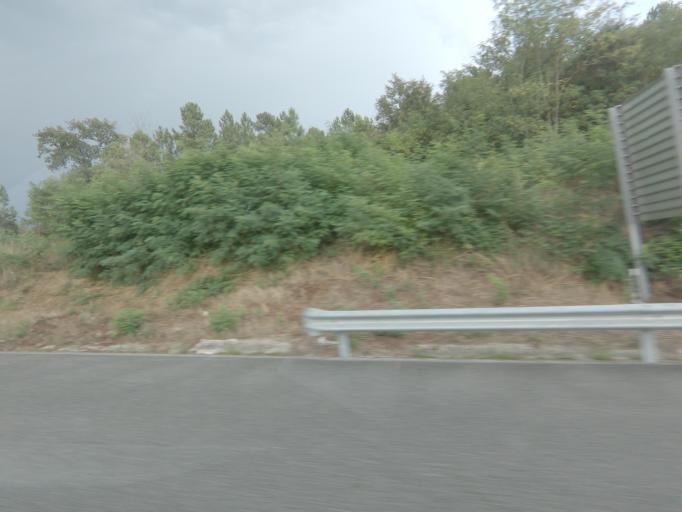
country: PT
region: Viseu
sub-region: Viseu
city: Abraveses
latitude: 40.6521
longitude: -7.9667
